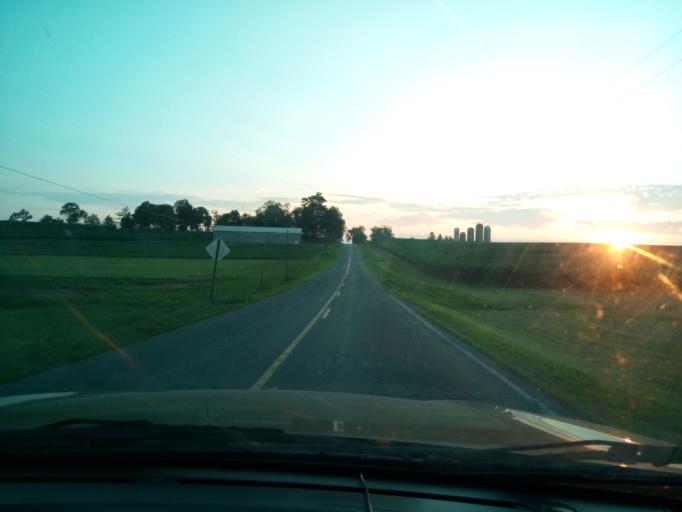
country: US
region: New York
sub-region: Wayne County
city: Clyde
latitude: 43.0205
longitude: -76.8090
